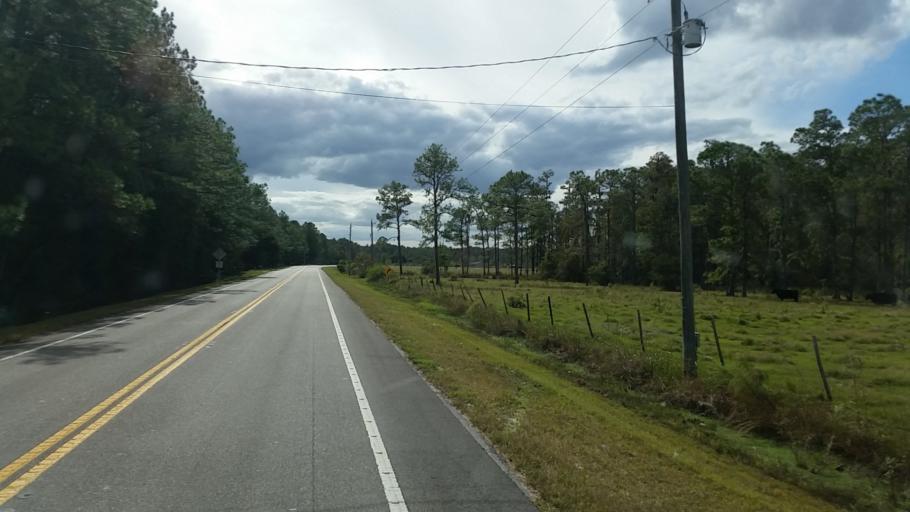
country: US
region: Florida
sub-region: Polk County
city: Gibsonia
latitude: 28.2576
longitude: -81.9597
